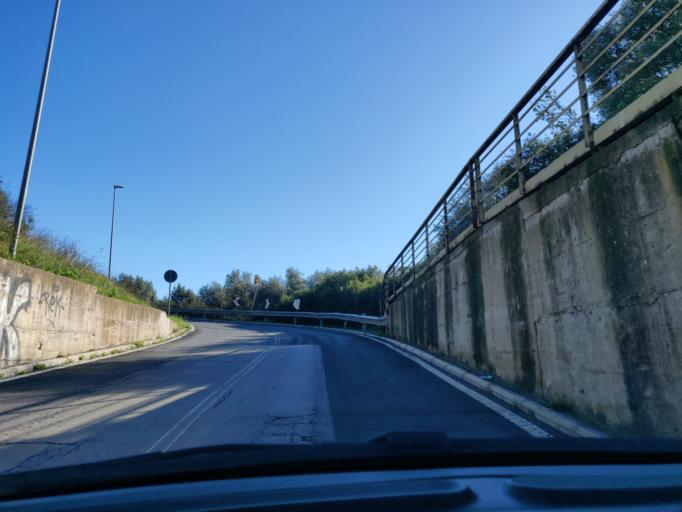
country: IT
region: Latium
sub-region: Citta metropolitana di Roma Capitale
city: Civitavecchia
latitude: 42.0953
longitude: 11.8186
